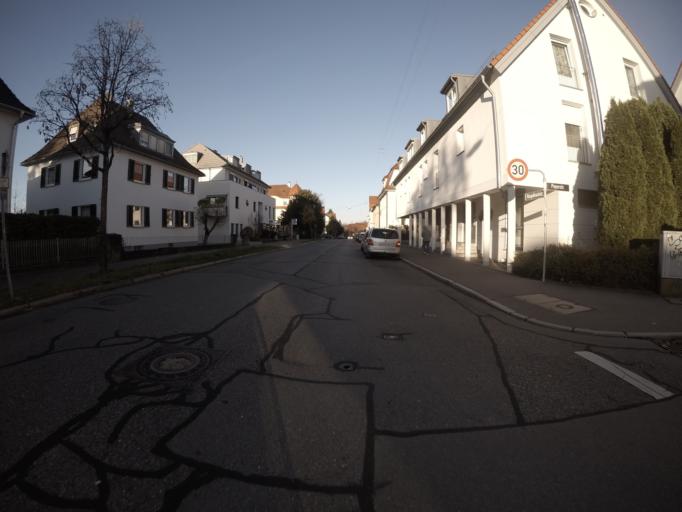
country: DE
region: Baden-Wuerttemberg
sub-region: Tuebingen Region
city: Reutlingen
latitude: 48.4843
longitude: 9.2121
